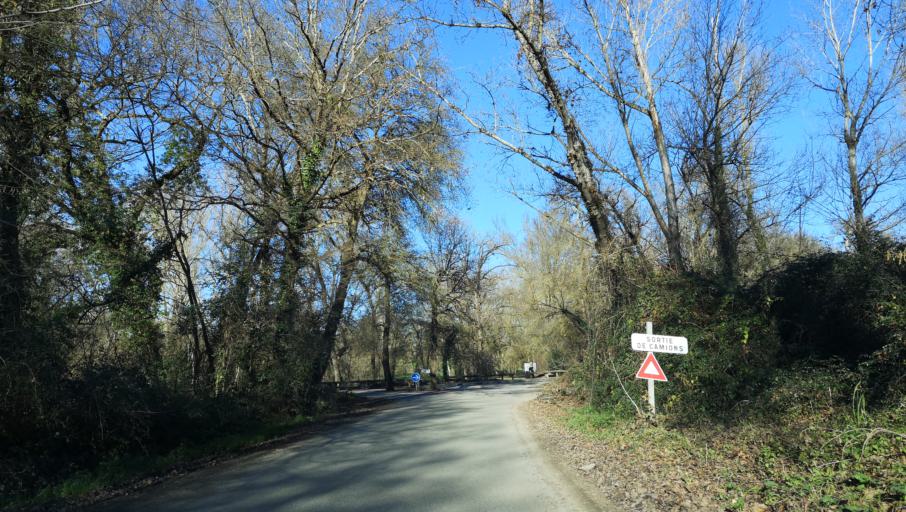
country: FR
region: Midi-Pyrenees
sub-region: Departement de la Haute-Garonne
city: Beauzelle
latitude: 43.6618
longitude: 1.3921
